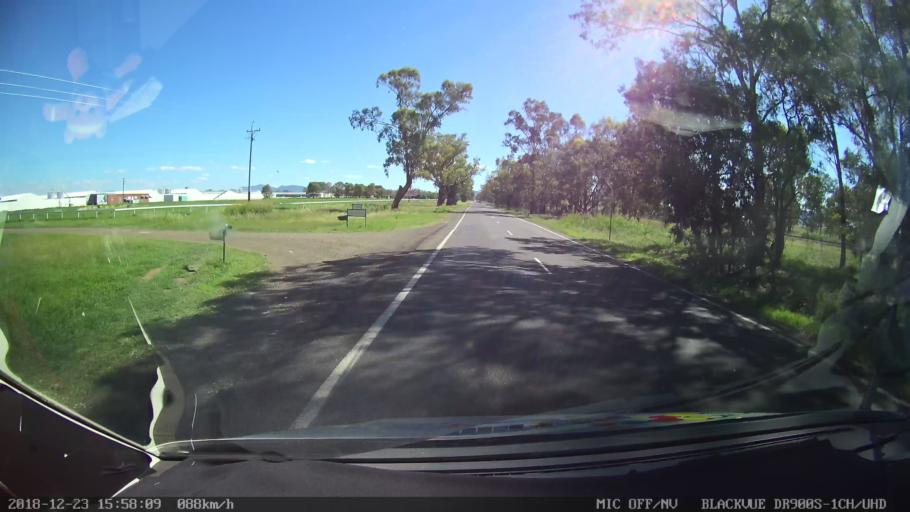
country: AU
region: New South Wales
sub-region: Tamworth Municipality
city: Phillip
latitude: -31.1850
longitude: 150.8441
